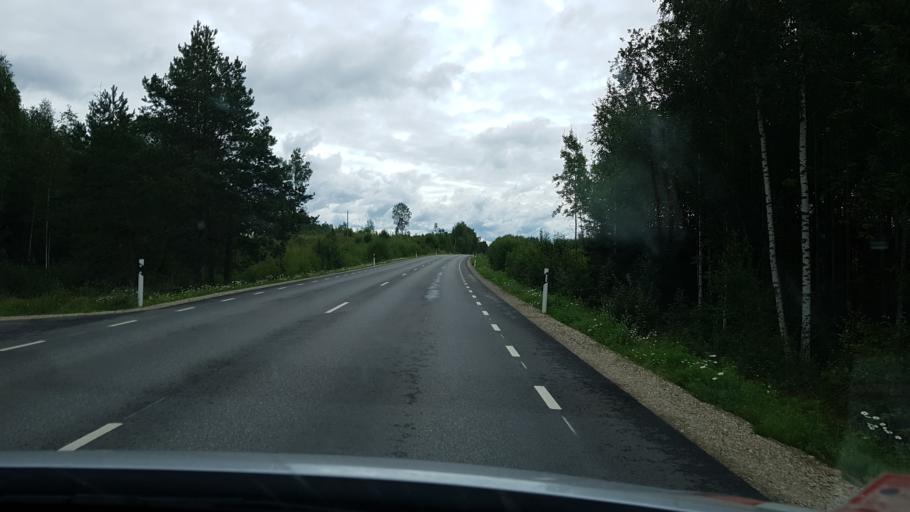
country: EE
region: Polvamaa
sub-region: Polva linn
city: Polva
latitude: 58.0085
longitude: 27.1945
